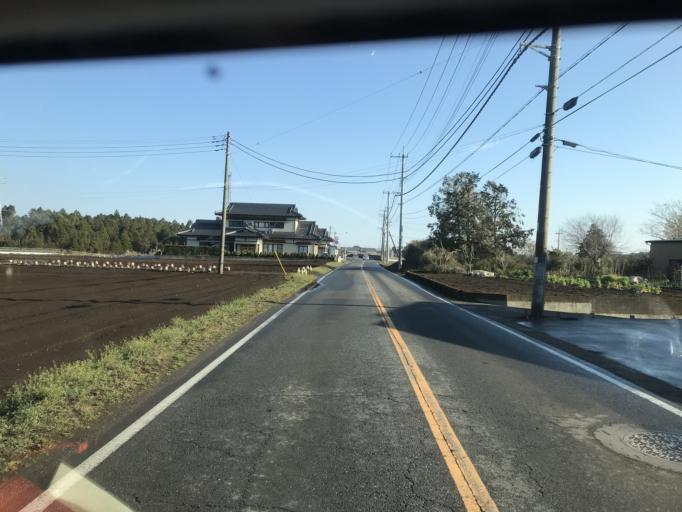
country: JP
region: Chiba
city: Sawara
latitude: 35.8478
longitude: 140.5089
